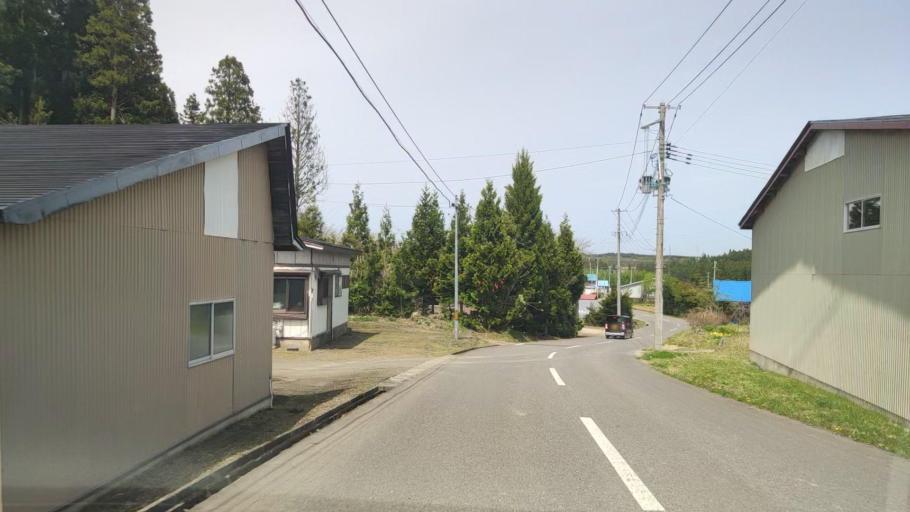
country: JP
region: Aomori
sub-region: Misawa Shi
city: Inuotose
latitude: 40.7766
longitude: 141.1218
